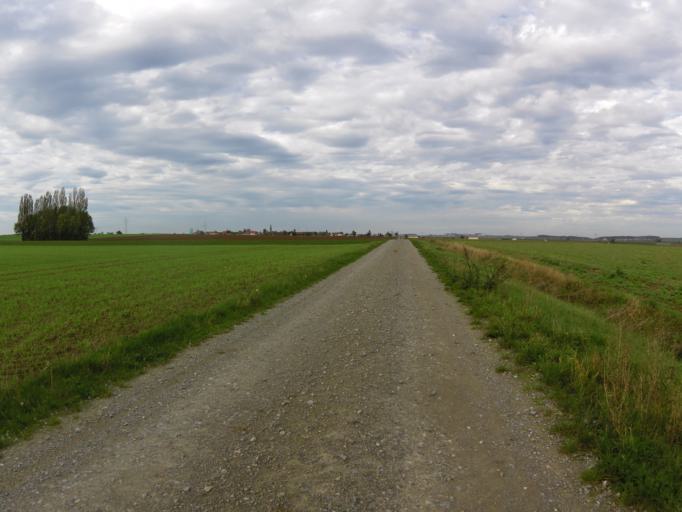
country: DE
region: Bavaria
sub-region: Regierungsbezirk Unterfranken
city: Biebelried
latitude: 49.7331
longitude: 10.0732
